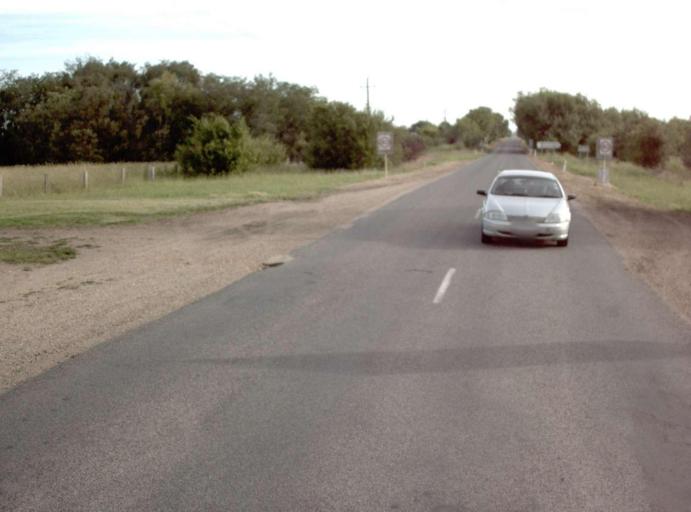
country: AU
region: Victoria
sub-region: Wellington
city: Heyfield
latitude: -37.9643
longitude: 146.8914
